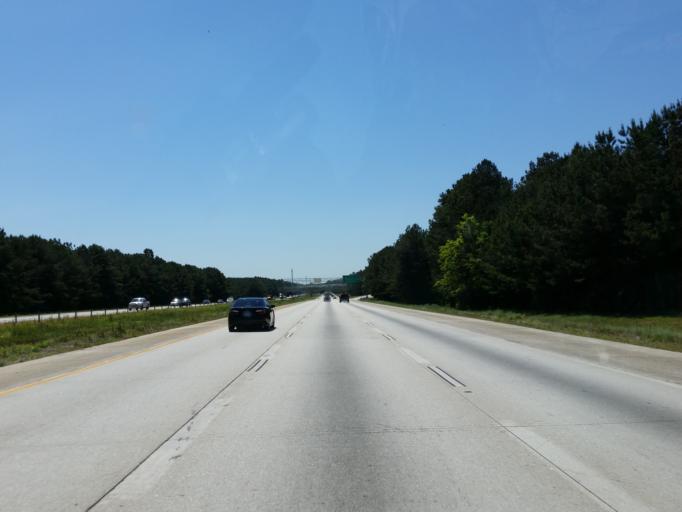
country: US
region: Georgia
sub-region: Clayton County
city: Conley
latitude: 33.6187
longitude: -84.2976
